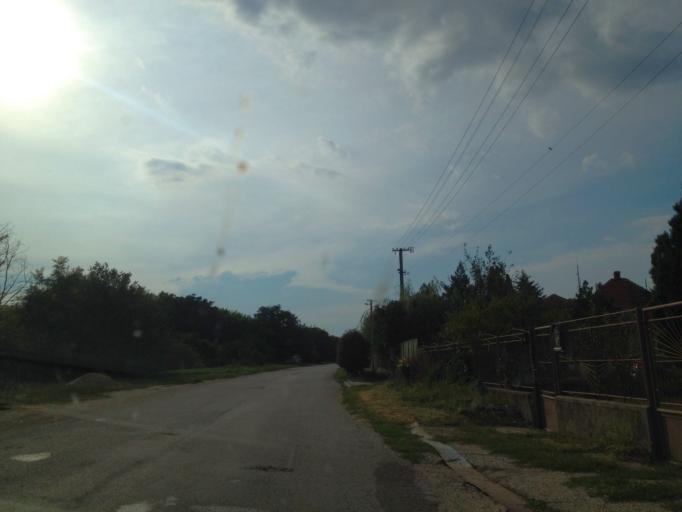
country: SK
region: Nitriansky
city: Svodin
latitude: 47.8959
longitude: 18.4098
